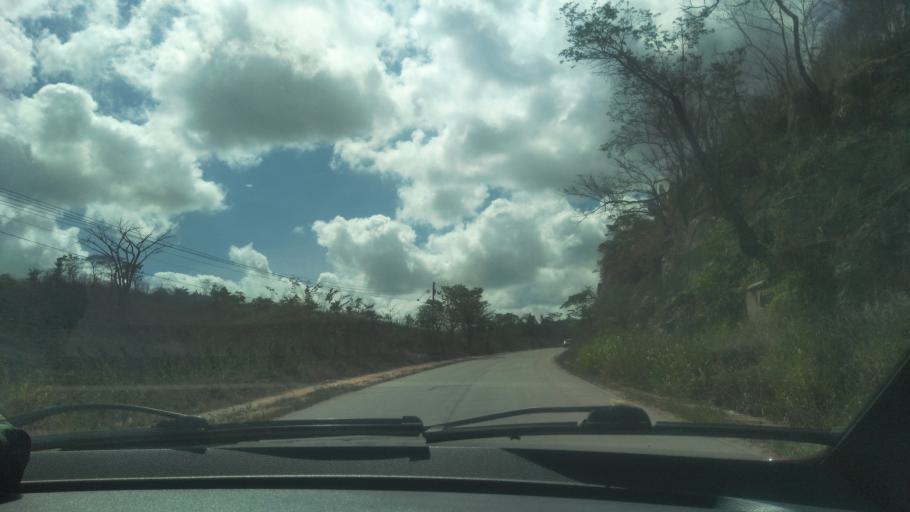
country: BR
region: Pernambuco
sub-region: Vitoria De Santo Antao
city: Vitoria de Santo Antao
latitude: -8.1352
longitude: -35.2775
